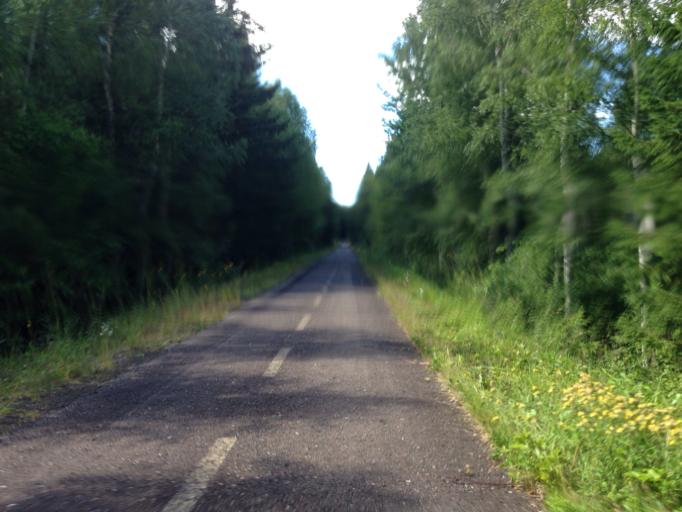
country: SE
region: Dalarna
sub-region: Ludvika Kommun
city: Ludvika
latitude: 60.2061
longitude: 15.0585
